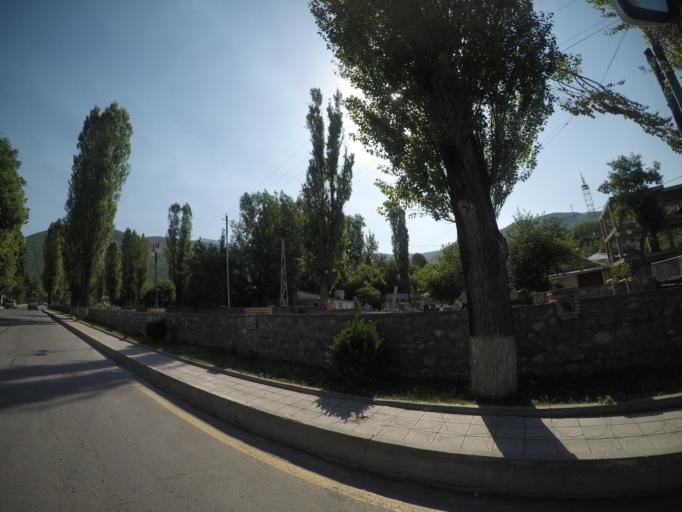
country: AZ
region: Shaki City
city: Sheki
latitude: 41.2007
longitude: 47.1792
